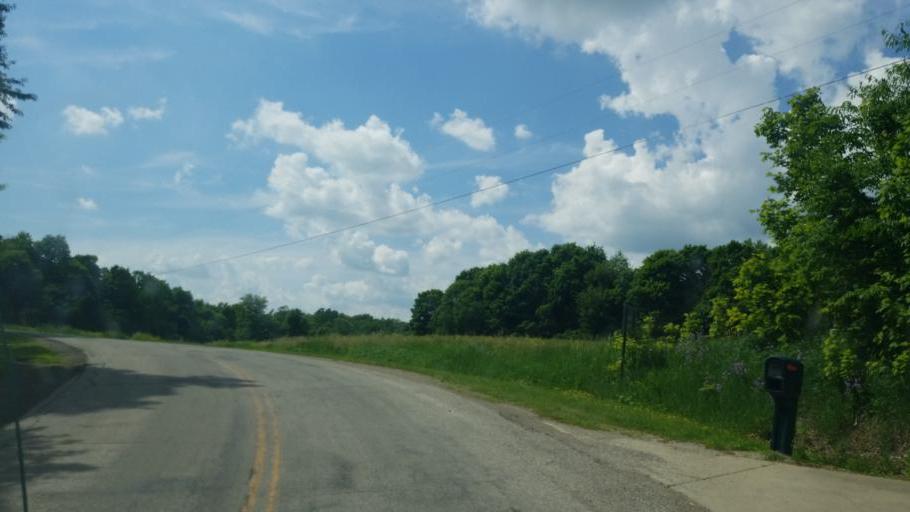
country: US
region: Ohio
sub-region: Sandusky County
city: Bellville
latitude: 40.6601
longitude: -82.4513
